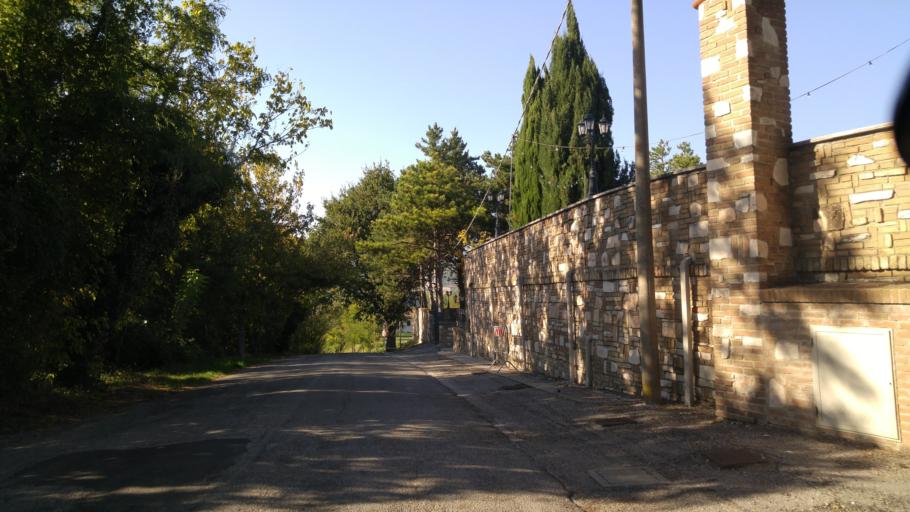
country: IT
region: The Marches
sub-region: Provincia di Pesaro e Urbino
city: Fermignano
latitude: 43.6592
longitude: 12.6446
